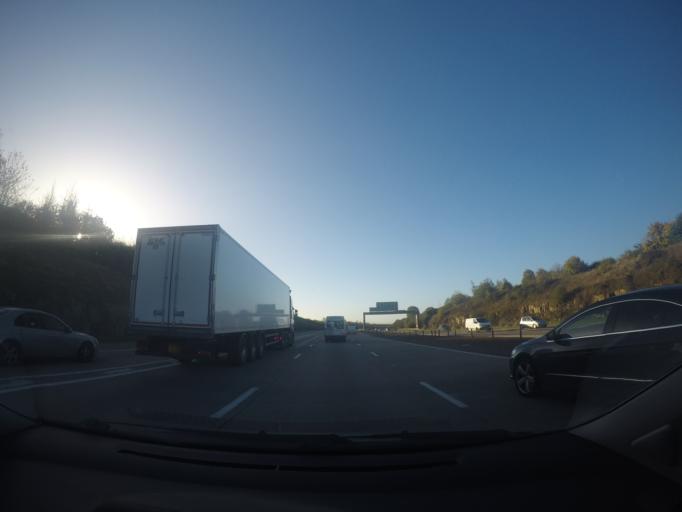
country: GB
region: England
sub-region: City and Borough of Leeds
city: Swillington
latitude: 53.7845
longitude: -1.4279
